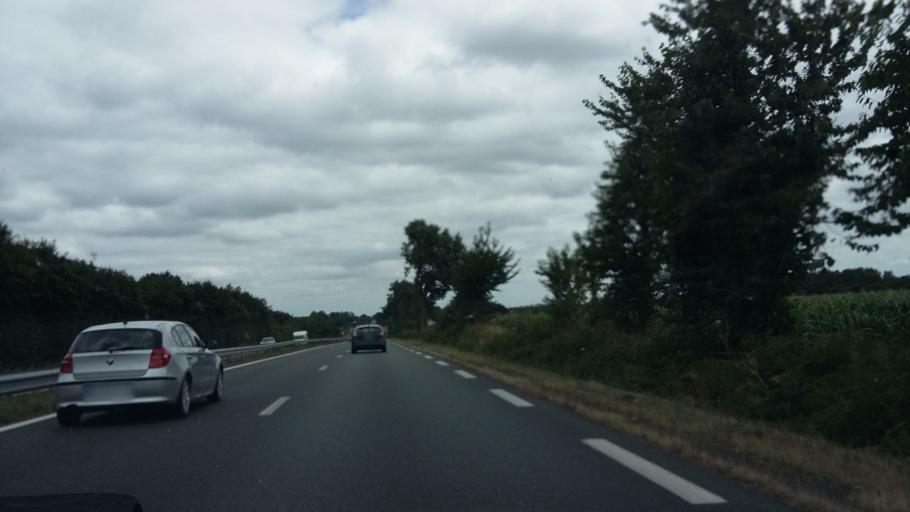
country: FR
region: Pays de la Loire
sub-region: Departement de la Vendee
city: Venansault
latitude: 46.7046
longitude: -1.5072
